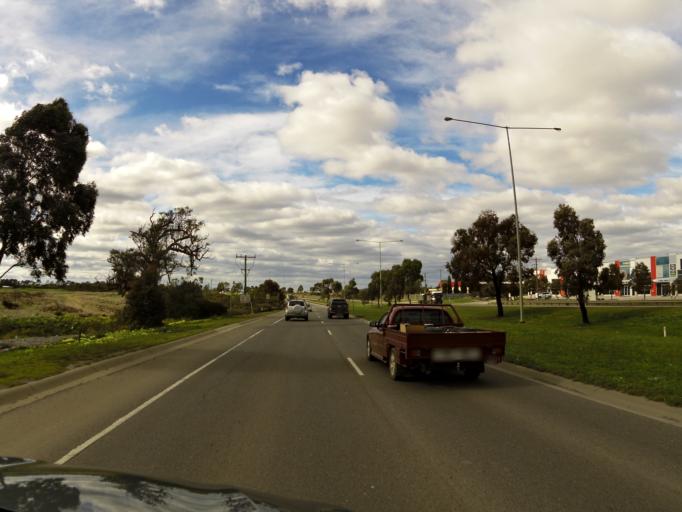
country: AU
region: Victoria
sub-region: Hume
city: Coolaroo
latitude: -37.6460
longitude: 144.9713
